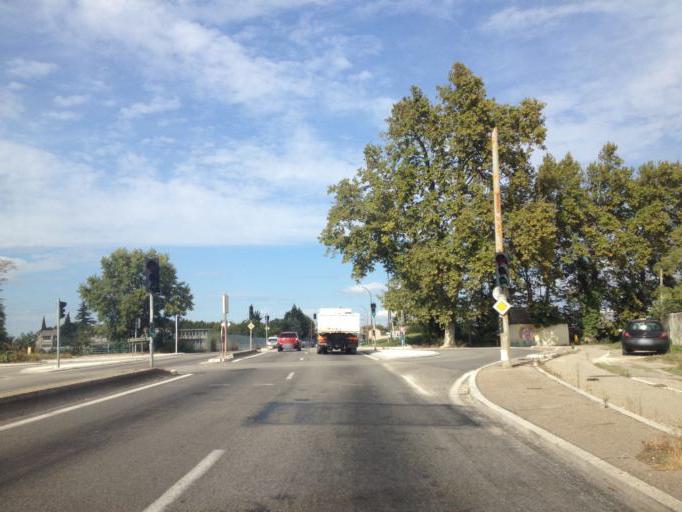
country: FR
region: Provence-Alpes-Cote d'Azur
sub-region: Departement du Vaucluse
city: Sorgues
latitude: 43.9894
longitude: 4.8629
